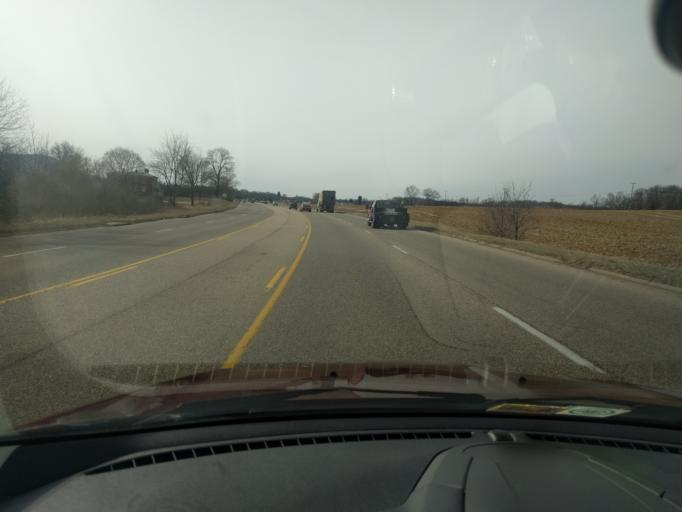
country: US
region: Virginia
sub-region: Augusta County
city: Stuarts Draft
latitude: 38.0414
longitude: -79.0179
